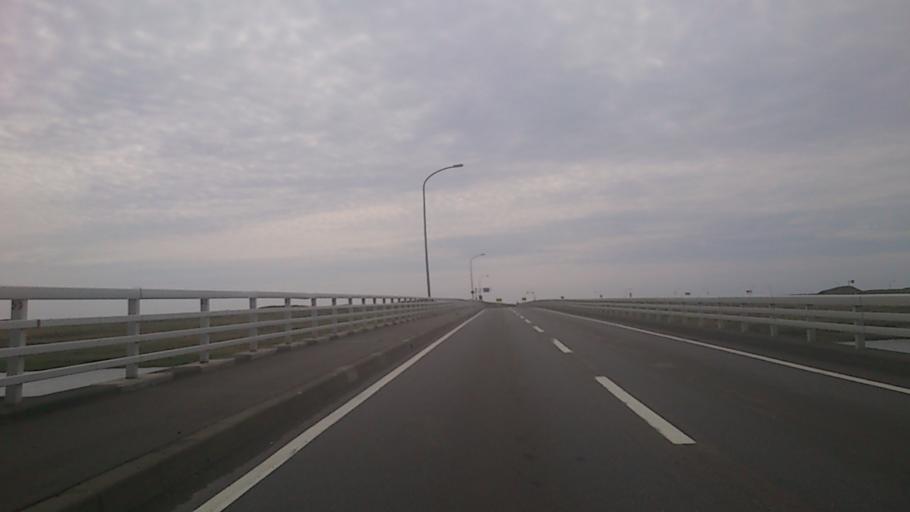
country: JP
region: Hokkaido
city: Makubetsu
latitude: 44.9237
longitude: 141.7287
